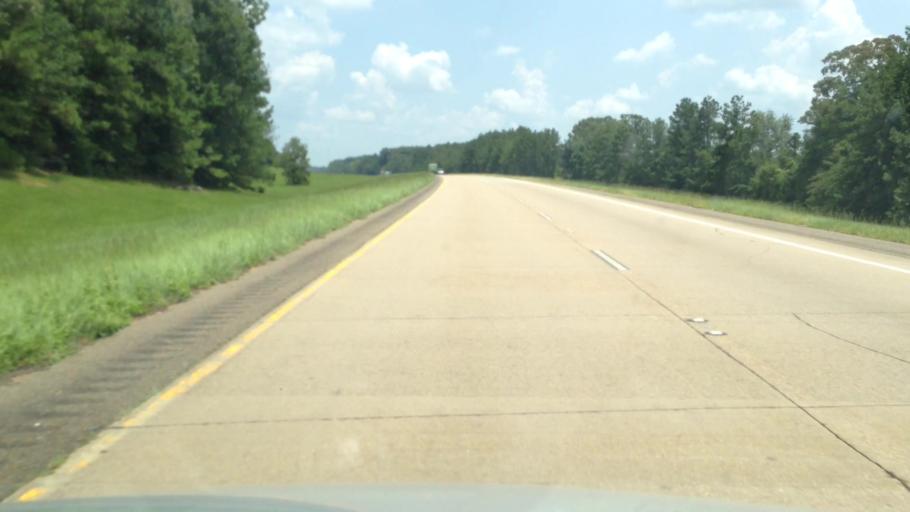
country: US
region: Louisiana
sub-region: Rapides Parish
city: Lecompte
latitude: 31.0300
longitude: -92.4077
